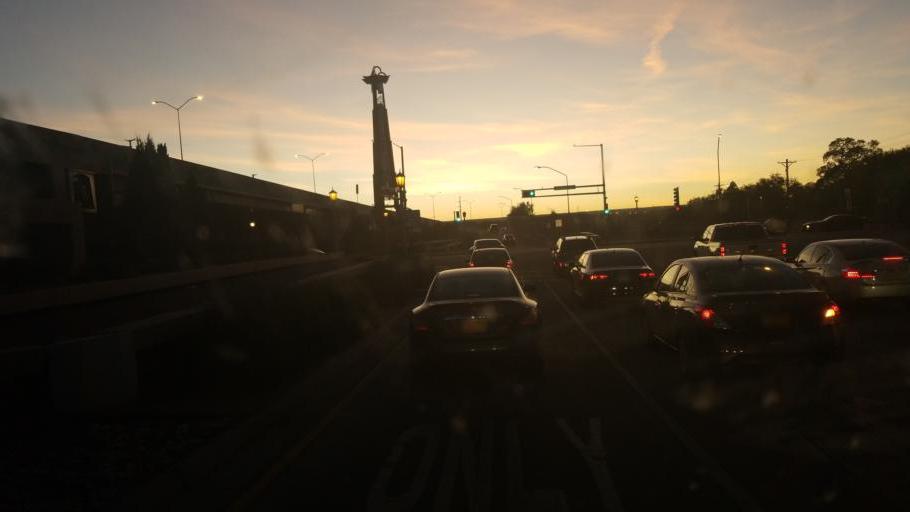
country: US
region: New Mexico
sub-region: Bernalillo County
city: Albuquerque
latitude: 35.1056
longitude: -106.6702
